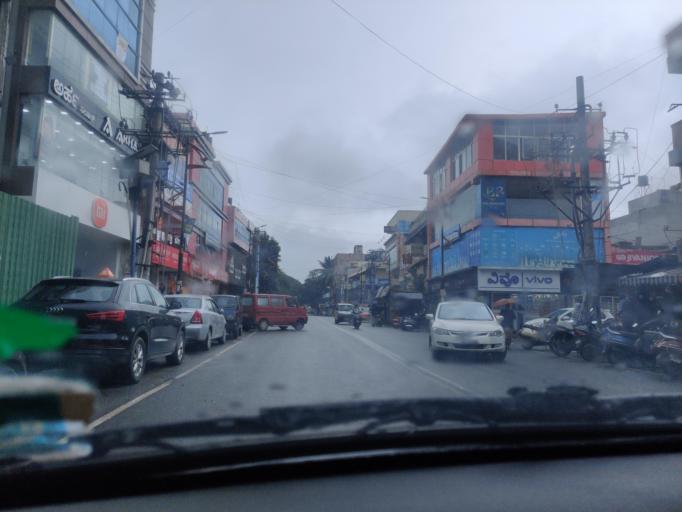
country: IN
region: Karnataka
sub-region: Bangalore Urban
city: Bangalore
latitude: 13.0164
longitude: 77.6362
